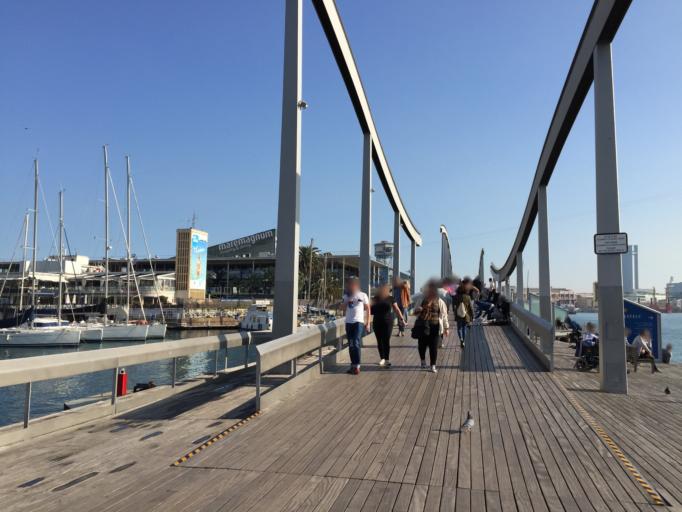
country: ES
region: Catalonia
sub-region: Provincia de Barcelona
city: Ciutat Vella
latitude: 41.3754
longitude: 2.1802
